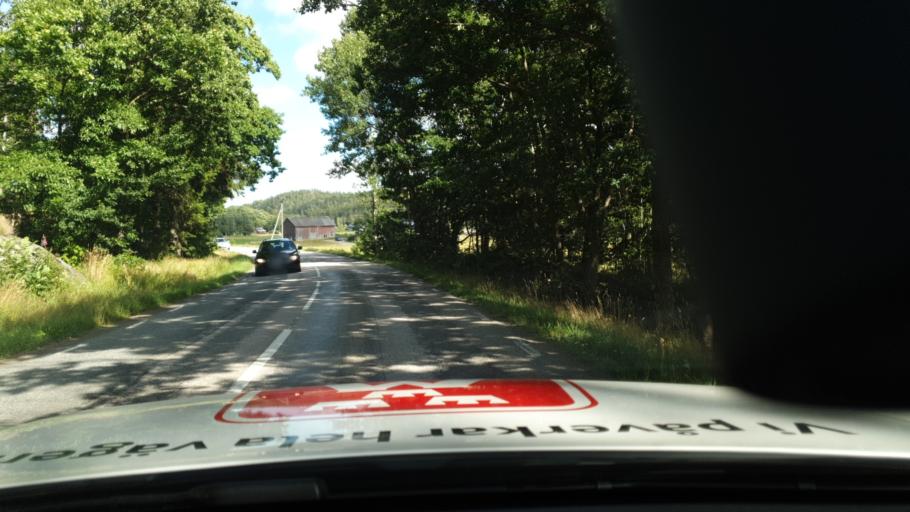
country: SE
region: Vaestra Goetaland
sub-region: Orust
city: Henan
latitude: 58.2259
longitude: 11.6306
